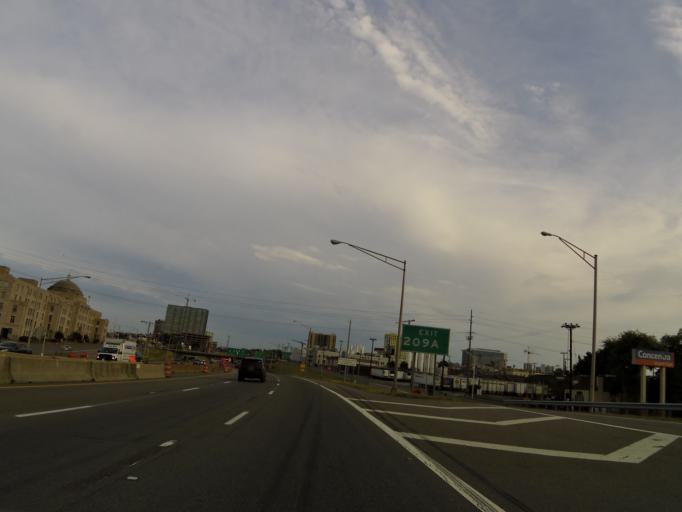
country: US
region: Tennessee
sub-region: Davidson County
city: Nashville
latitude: 36.1606
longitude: -86.7931
